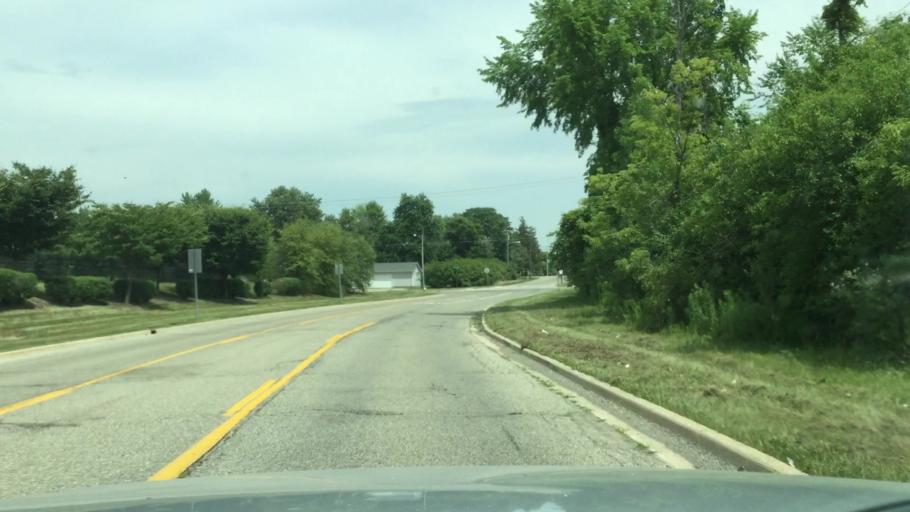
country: US
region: Michigan
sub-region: Genesee County
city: Flint
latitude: 42.9984
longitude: -83.7638
